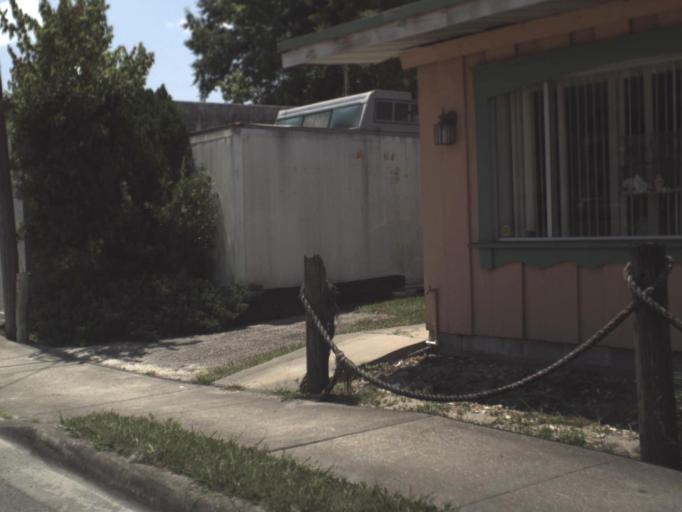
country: US
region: Florida
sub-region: Citrus County
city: Crystal River
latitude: 28.8990
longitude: -82.5878
